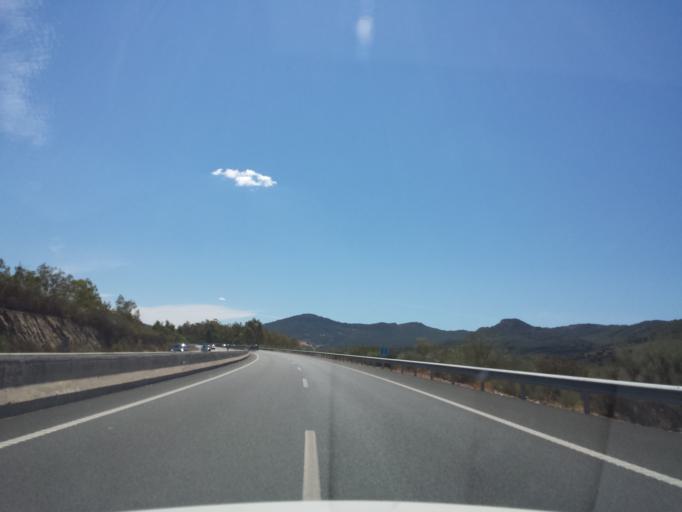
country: ES
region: Extremadura
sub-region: Provincia de Caceres
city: Romangordo
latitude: 39.7167
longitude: -5.7070
